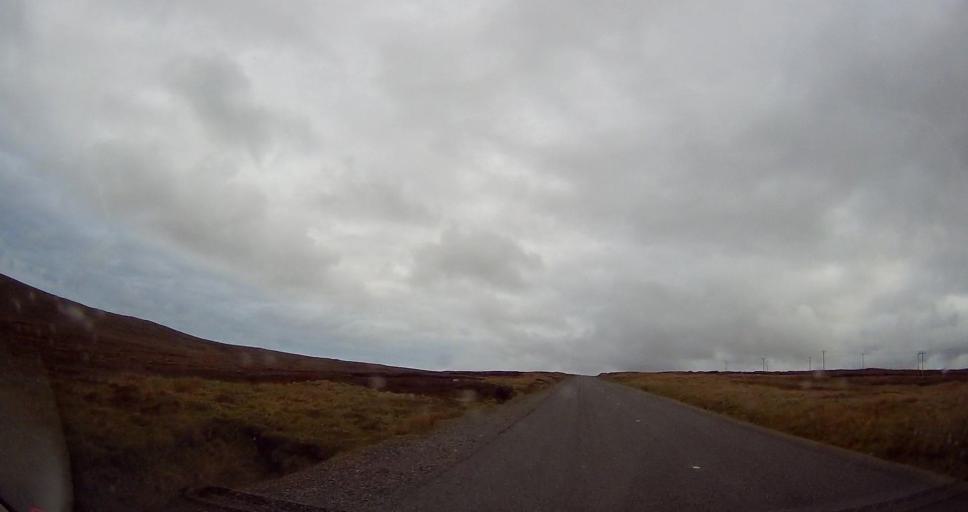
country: GB
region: Scotland
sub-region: Shetland Islands
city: Shetland
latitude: 60.6208
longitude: -1.0748
